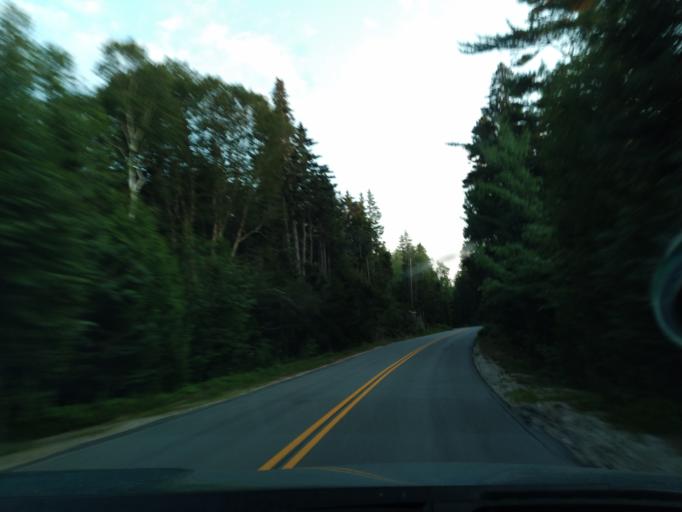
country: US
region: Maine
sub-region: Hancock County
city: Gouldsboro
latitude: 44.3779
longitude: -68.0688
